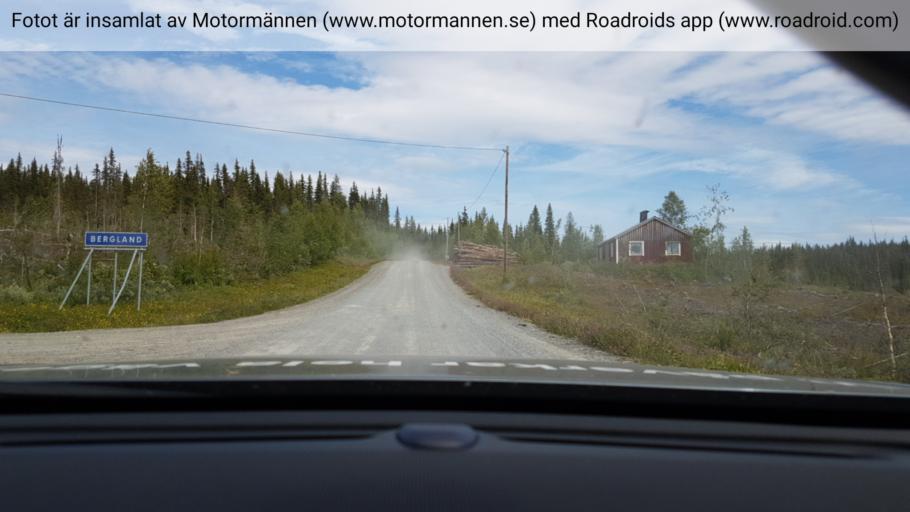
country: SE
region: Vaesterbotten
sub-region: Vilhelmina Kommun
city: Sjoberg
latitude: 65.1986
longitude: 16.1382
